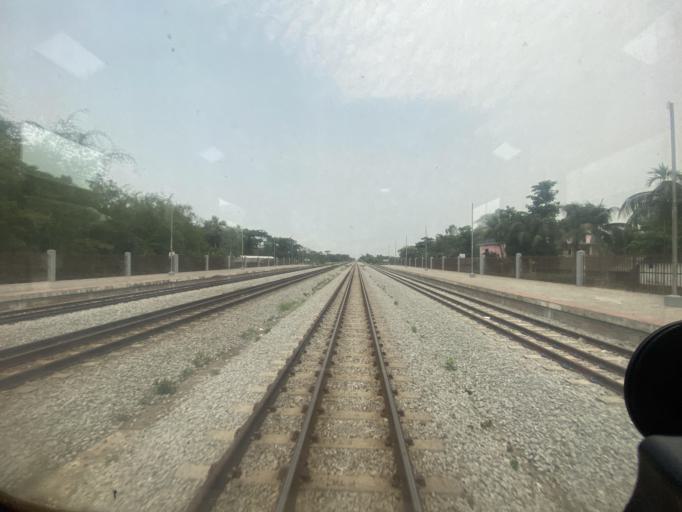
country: BD
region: Chittagong
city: Laksham
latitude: 23.3068
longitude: 91.1385
